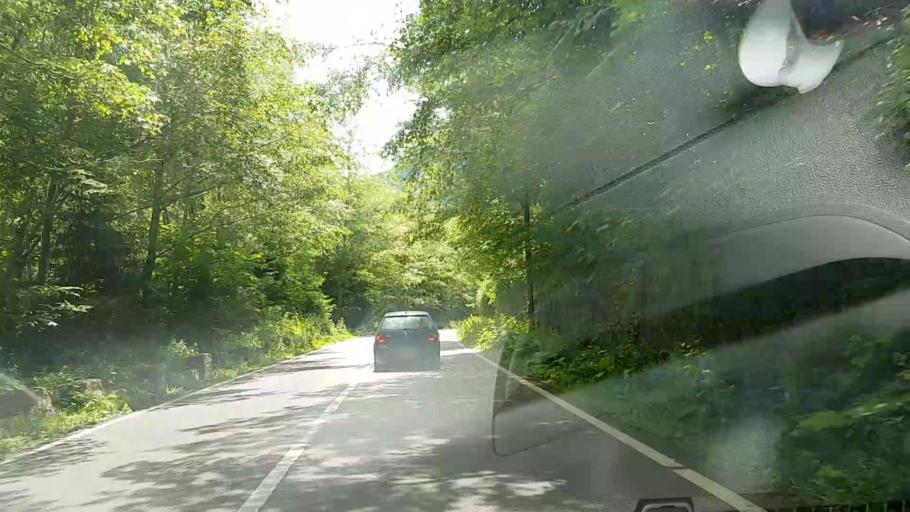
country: RO
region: Suceava
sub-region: Comuna Crucea
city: Crucea
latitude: 47.2969
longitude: 25.6323
